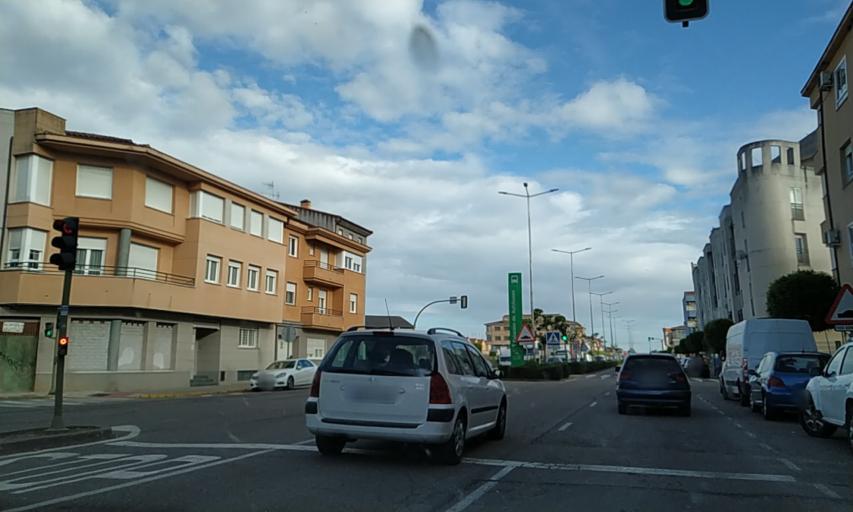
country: ES
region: Extremadura
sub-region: Provincia de Caceres
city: Moraleja
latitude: 40.0668
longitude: -6.6544
